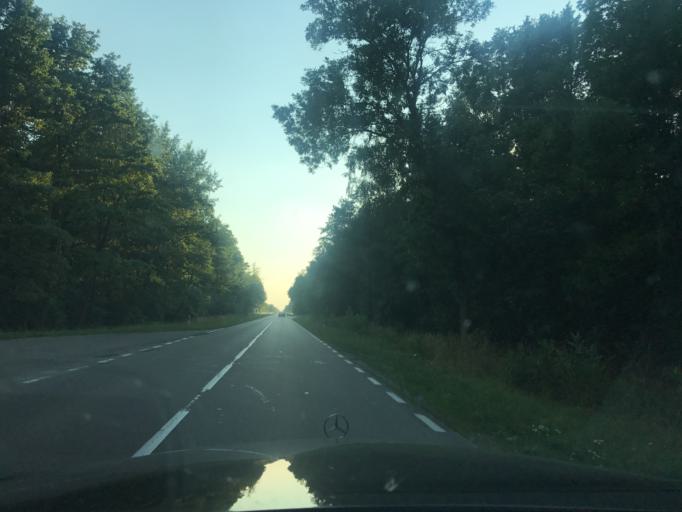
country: PL
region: Lublin Voivodeship
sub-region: Powiat parczewski
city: Debowa Kloda
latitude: 51.6452
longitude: 22.9679
